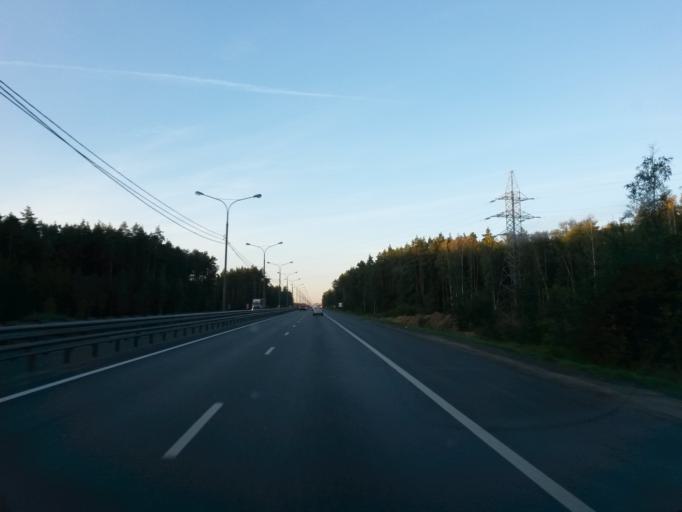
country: RU
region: Moskovskaya
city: Kostino
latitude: 56.0360
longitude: 37.8899
